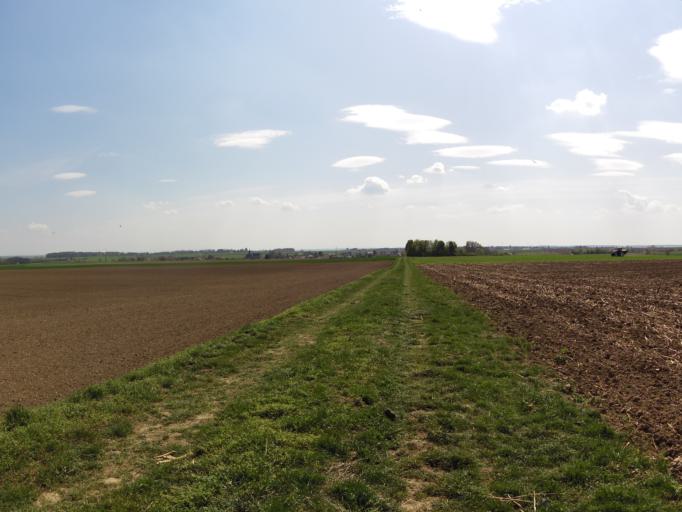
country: DE
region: Bavaria
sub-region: Regierungsbezirk Unterfranken
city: Giebelstadt
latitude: 49.6808
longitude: 9.9561
